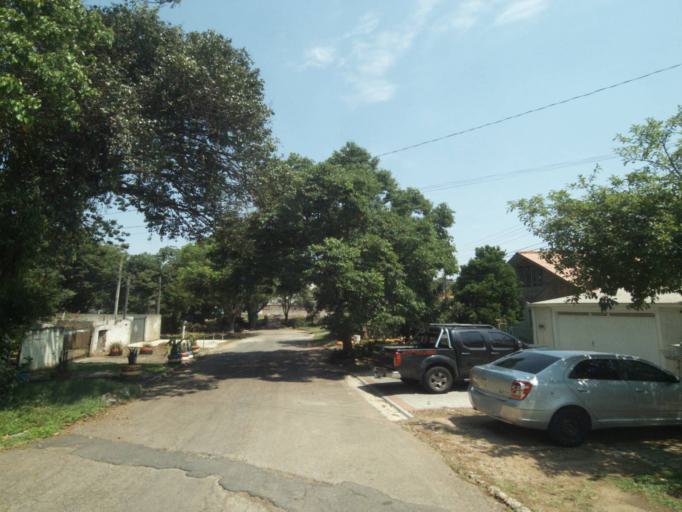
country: BR
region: Parana
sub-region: Sao Jose Dos Pinhais
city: Sao Jose dos Pinhais
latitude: -25.5184
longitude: -49.2695
